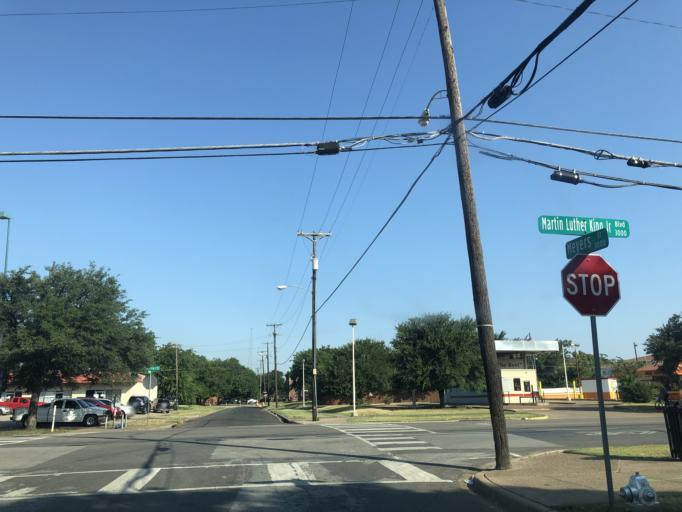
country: US
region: Texas
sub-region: Dallas County
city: Dallas
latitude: 32.7710
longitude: -96.7658
